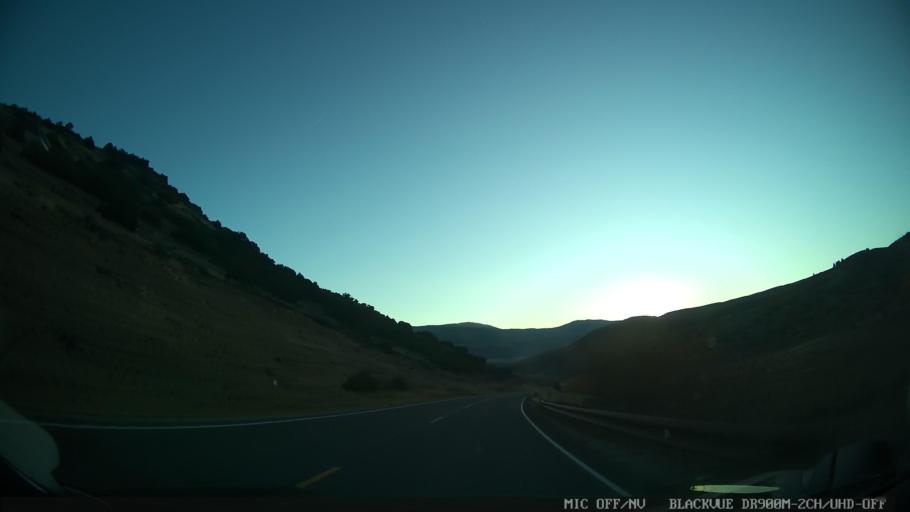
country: US
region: Colorado
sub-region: Eagle County
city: Edwards
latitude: 39.8168
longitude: -106.6609
